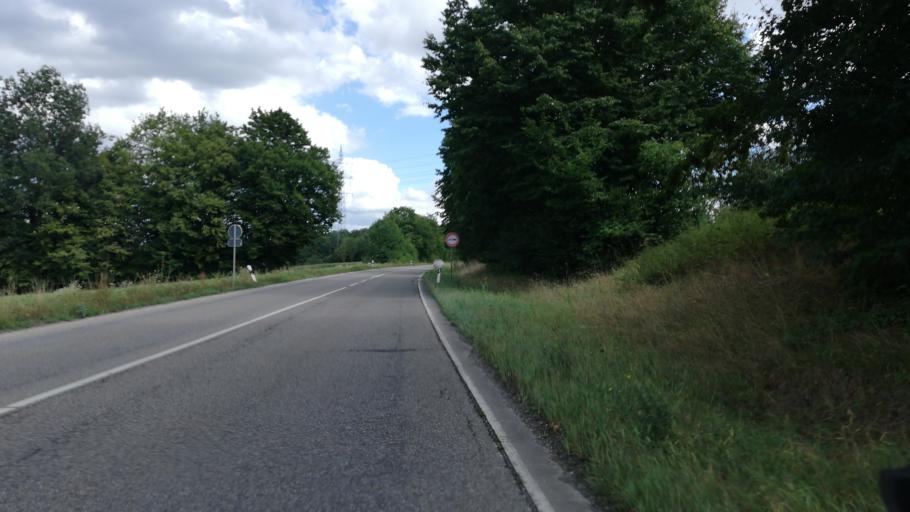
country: DE
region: Baden-Wuerttemberg
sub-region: Regierungsbezirk Stuttgart
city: Waiblingen
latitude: 48.8646
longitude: 9.2814
